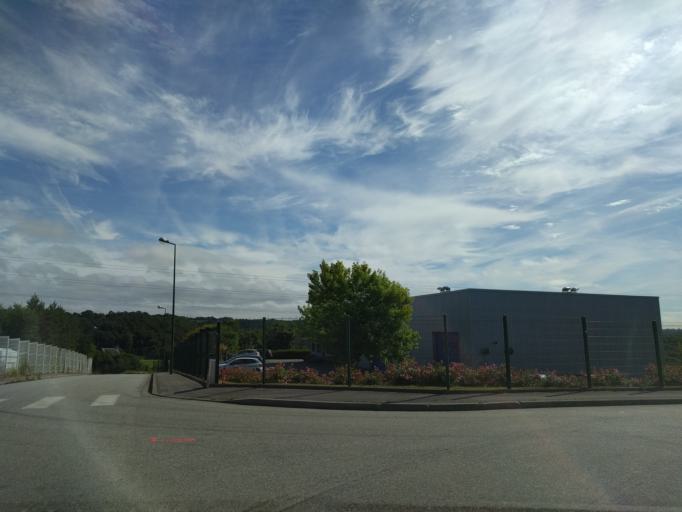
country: FR
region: Brittany
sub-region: Departement du Finistere
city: Quimper
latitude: 48.0094
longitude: -4.0715
